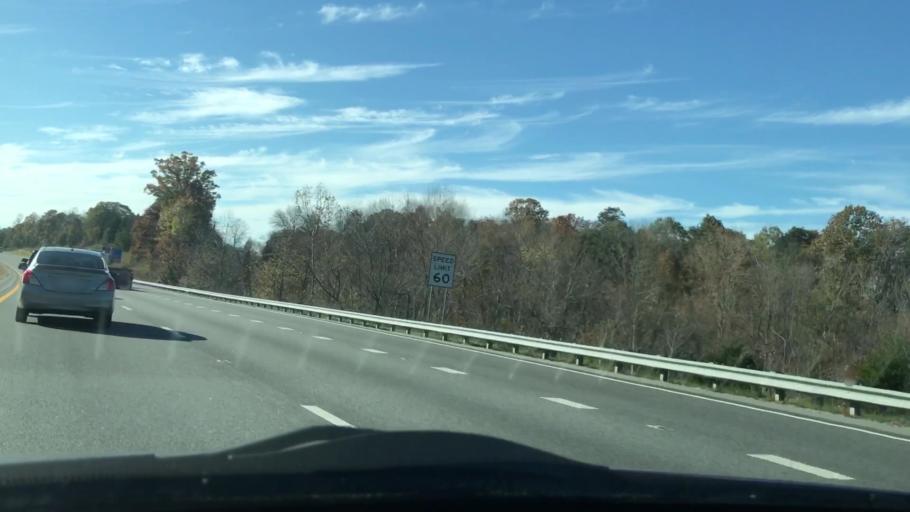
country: US
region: North Carolina
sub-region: Guilford County
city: High Point
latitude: 36.0095
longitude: -80.0168
